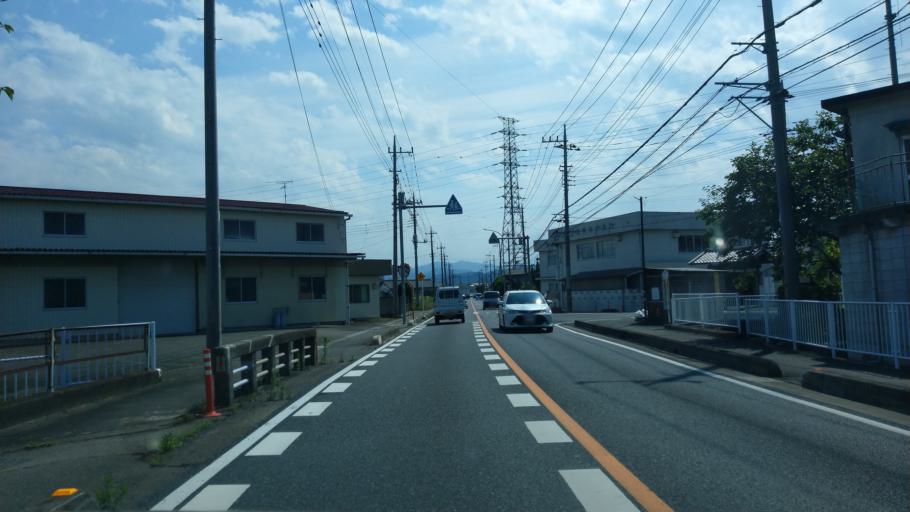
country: JP
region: Saitama
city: Honjo
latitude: 36.2153
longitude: 139.1592
